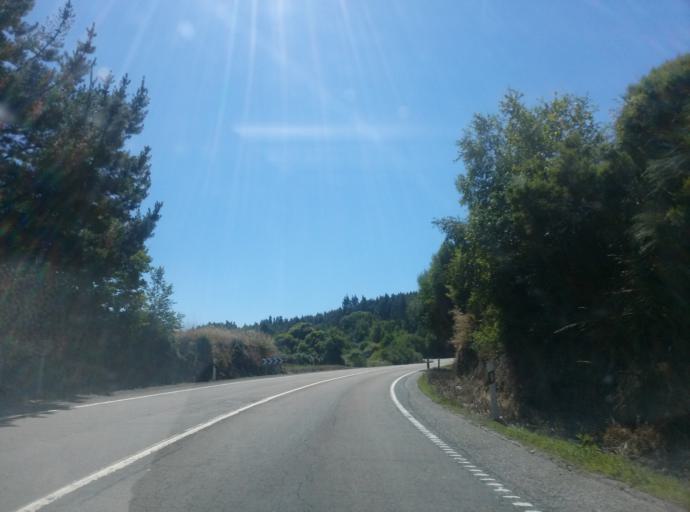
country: ES
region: Galicia
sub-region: Provincia de Lugo
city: Castro de Rei
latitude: 43.1621
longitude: -7.3799
